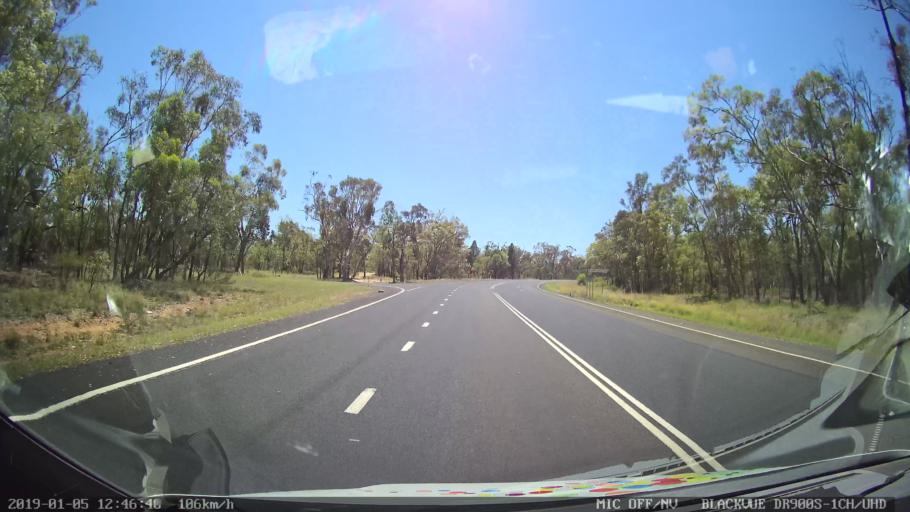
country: AU
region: New South Wales
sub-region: Warrumbungle Shire
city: Coonabarabran
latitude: -31.1156
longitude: 149.5656
